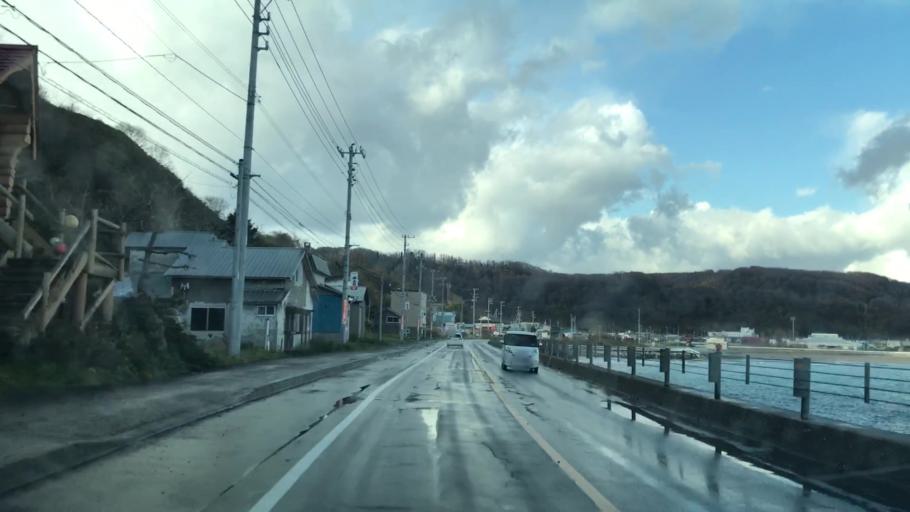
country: JP
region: Hokkaido
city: Yoichi
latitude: 43.2951
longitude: 140.6107
